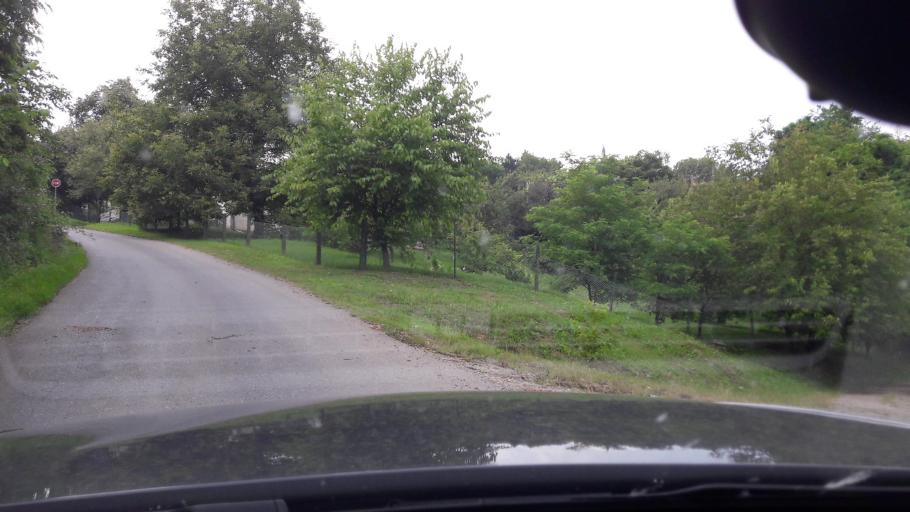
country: RS
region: Central Serbia
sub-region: Belgrade
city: Grocka
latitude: 44.6531
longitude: 20.5964
